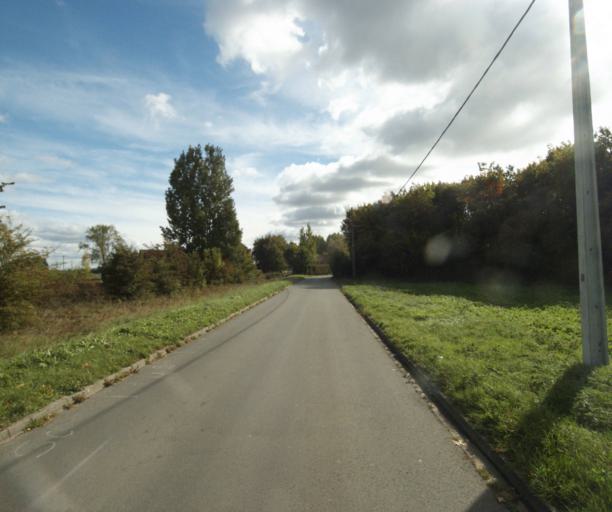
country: FR
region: Nord-Pas-de-Calais
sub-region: Departement du Nord
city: Armentieres
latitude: 50.6655
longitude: 2.8988
